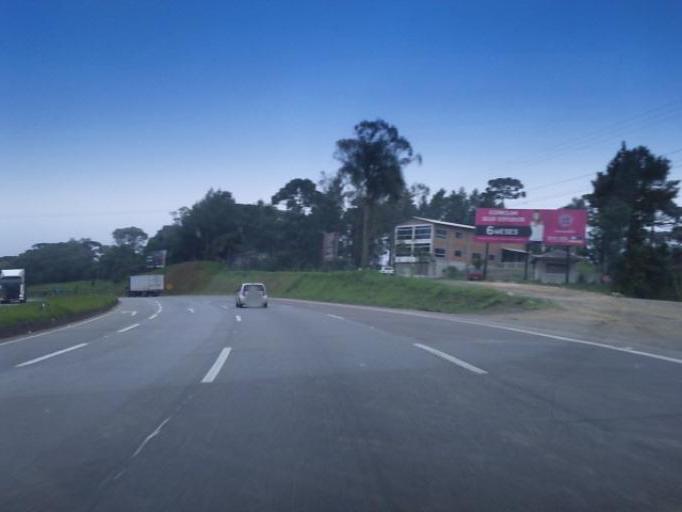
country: BR
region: Parana
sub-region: Sao Jose Dos Pinhais
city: Sao Jose dos Pinhais
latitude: -25.8469
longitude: -49.0646
